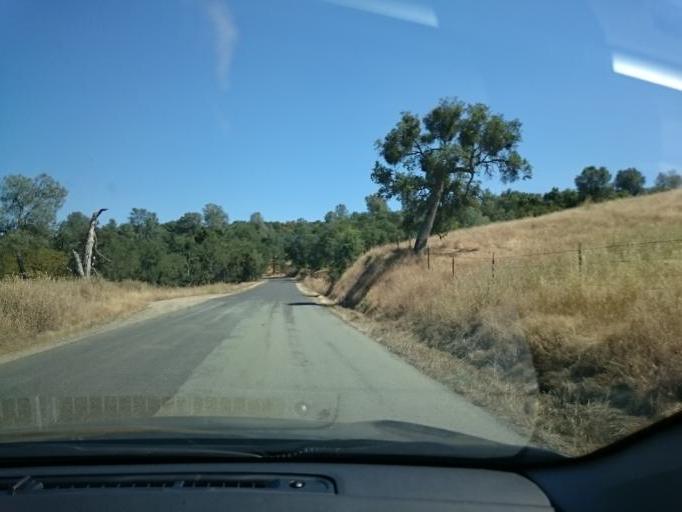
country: US
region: California
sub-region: Calaveras County
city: Rancho Calaveras
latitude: 38.1459
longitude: -120.8209
